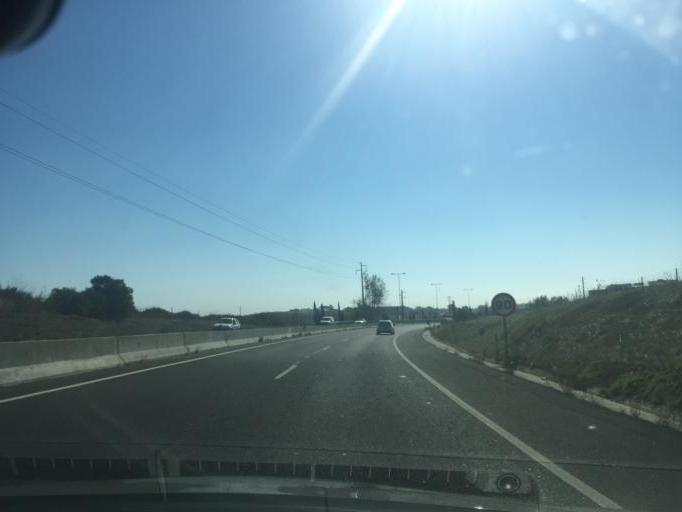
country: PT
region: Lisbon
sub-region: Oeiras
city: Porto Salvo
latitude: 38.7311
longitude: -9.2966
